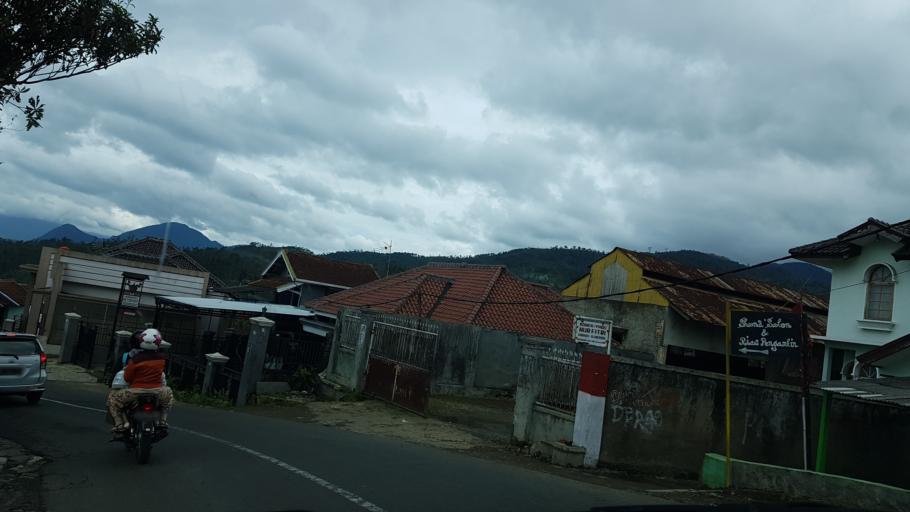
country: ID
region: West Java
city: Banjar
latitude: -7.1235
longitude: 107.4314
